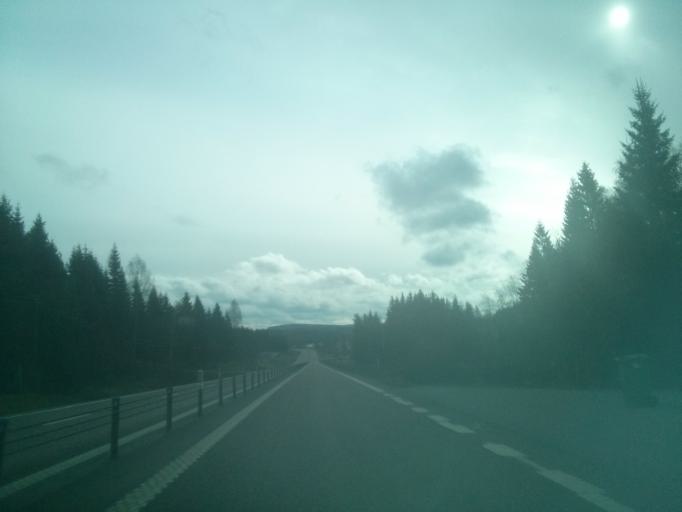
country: SE
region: Vaesternorrland
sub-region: Timra Kommun
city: Soraker
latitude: 62.5513
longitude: 17.6229
